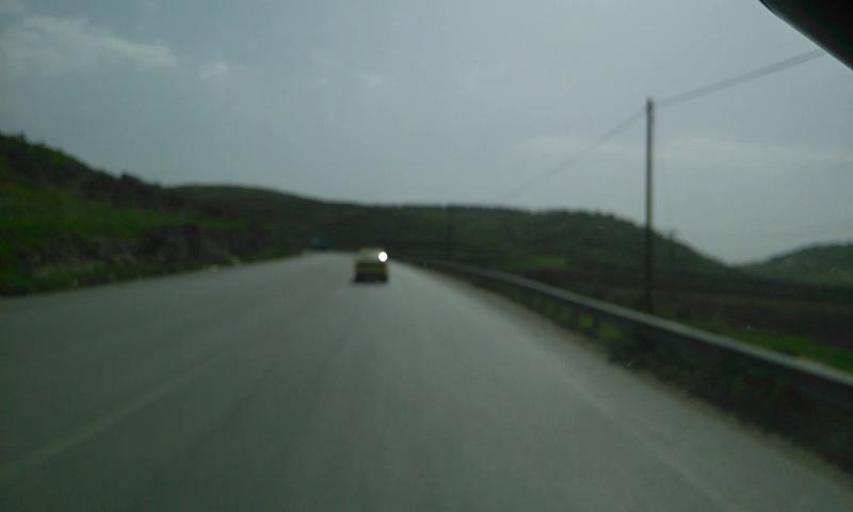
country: PS
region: West Bank
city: `Arrabah
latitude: 32.3871
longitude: 35.2150
